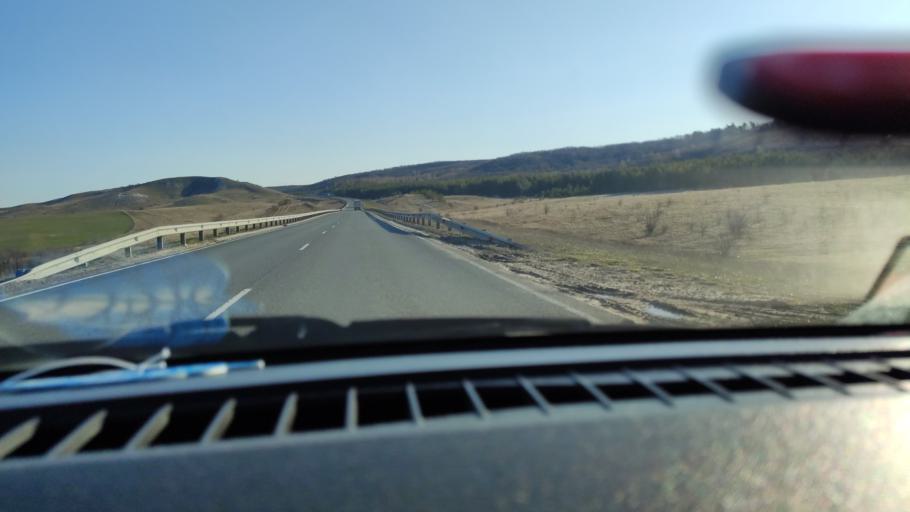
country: RU
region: Saratov
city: Alekseyevka
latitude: 52.3642
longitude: 47.9591
